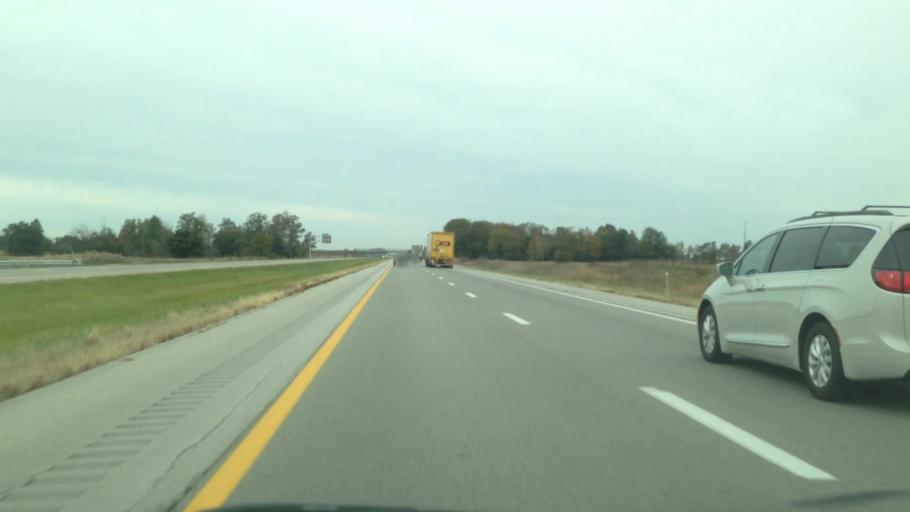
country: US
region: Ohio
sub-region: Fulton County
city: Wauseon
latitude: 41.5910
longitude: -84.1817
